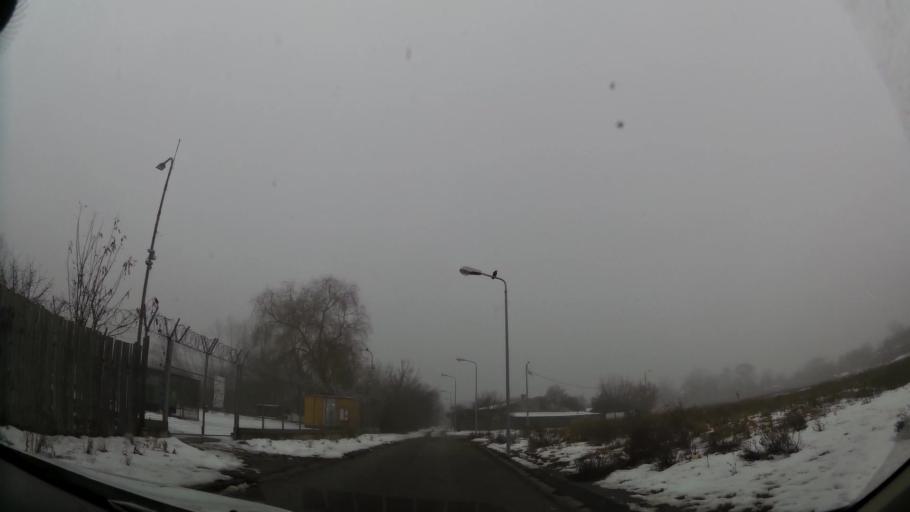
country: RO
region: Ilfov
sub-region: Comuna Chiajna
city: Rosu
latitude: 44.4698
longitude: 26.0144
